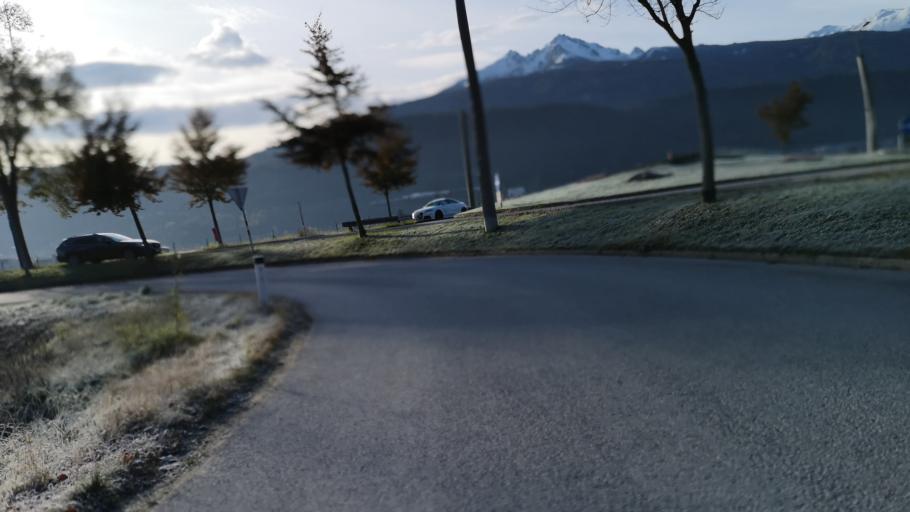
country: AT
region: Tyrol
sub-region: Politischer Bezirk Innsbruck Land
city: Vols
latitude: 47.2626
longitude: 11.3396
